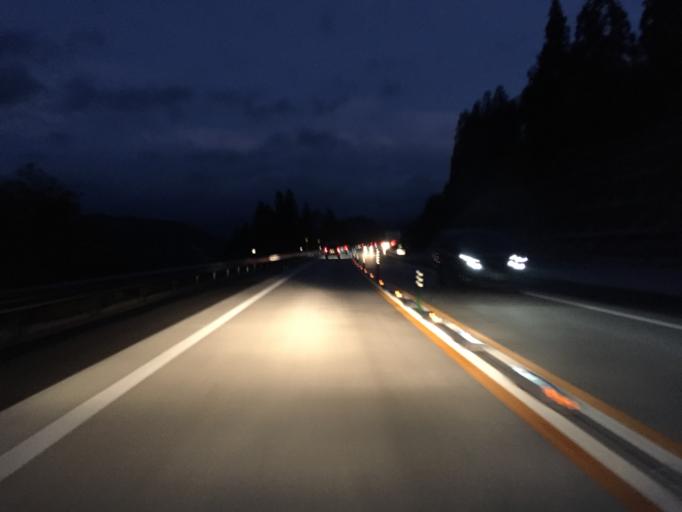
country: JP
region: Yamagata
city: Yonezawa
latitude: 37.8925
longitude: 140.1665
